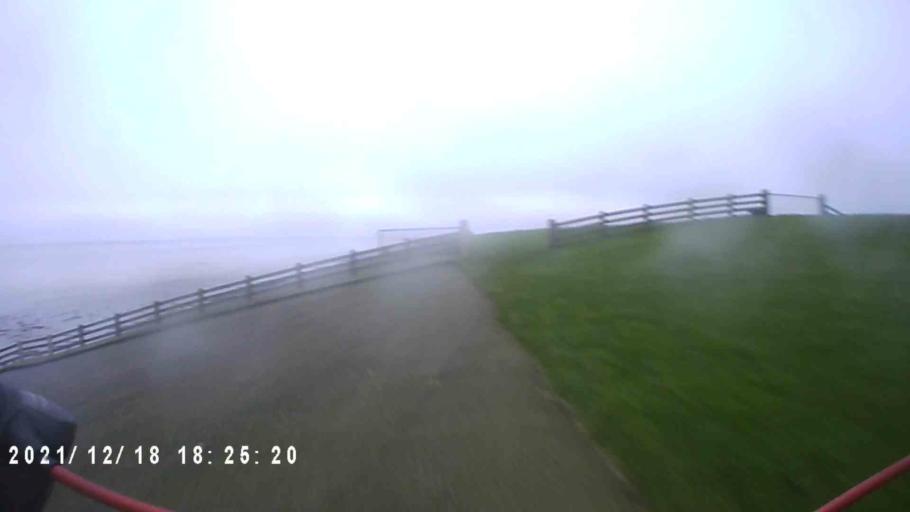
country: NL
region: Friesland
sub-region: Gemeente Dongeradeel
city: Ternaard
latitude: 53.3992
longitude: 5.9986
